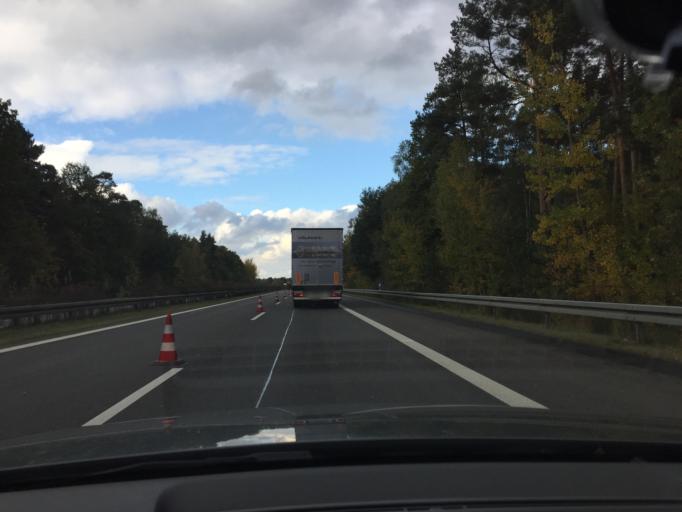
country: DE
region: Brandenburg
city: Bronkow
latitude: 51.6166
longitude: 13.9488
